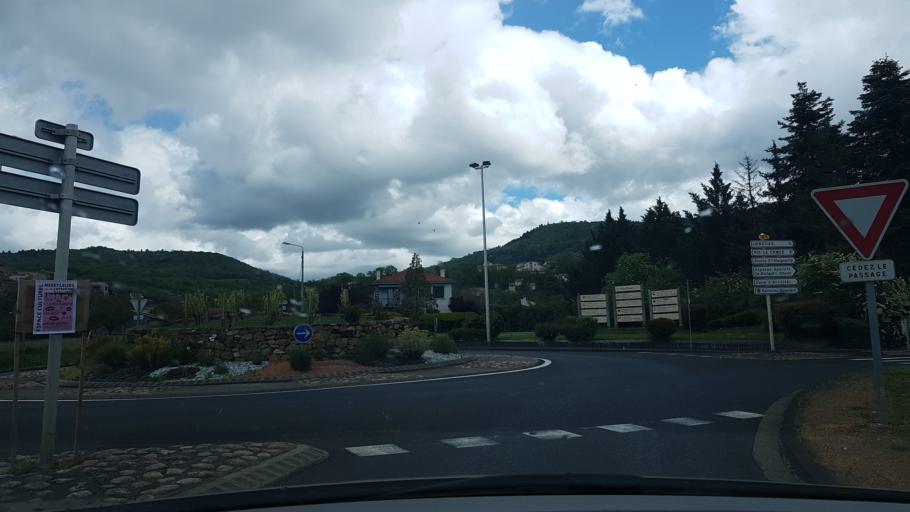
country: FR
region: Auvergne
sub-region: Departement du Puy-de-Dome
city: Mirefleurs
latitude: 45.6915
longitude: 3.2173
